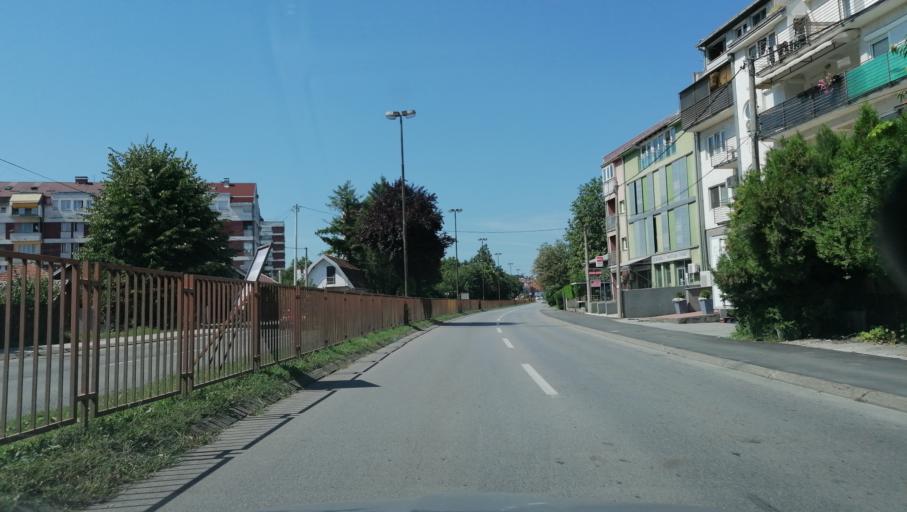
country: RS
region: Central Serbia
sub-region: Kolubarski Okrug
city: Valjevo
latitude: 44.2733
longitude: 19.8960
